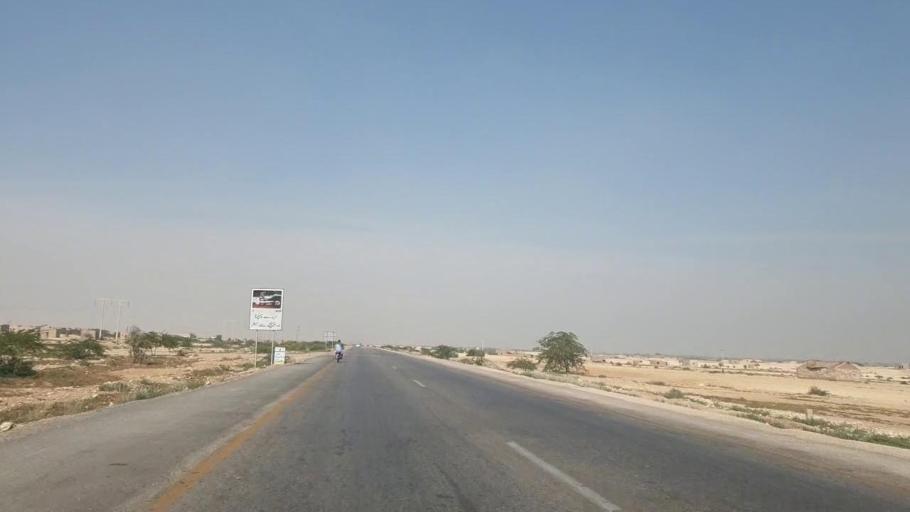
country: PK
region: Sindh
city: Hala
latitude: 25.8013
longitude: 68.2778
